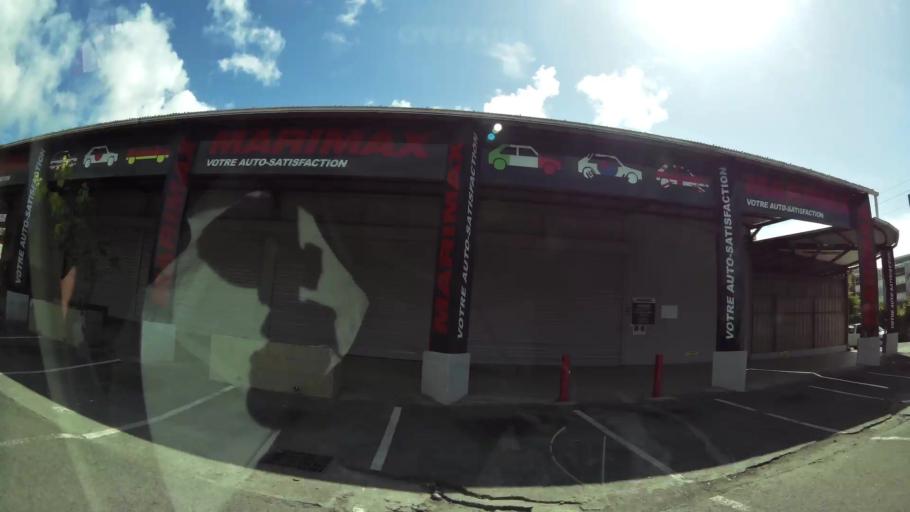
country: GP
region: Guadeloupe
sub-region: Guadeloupe
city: Pointe-a-Pitre
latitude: 16.2461
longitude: -61.5406
